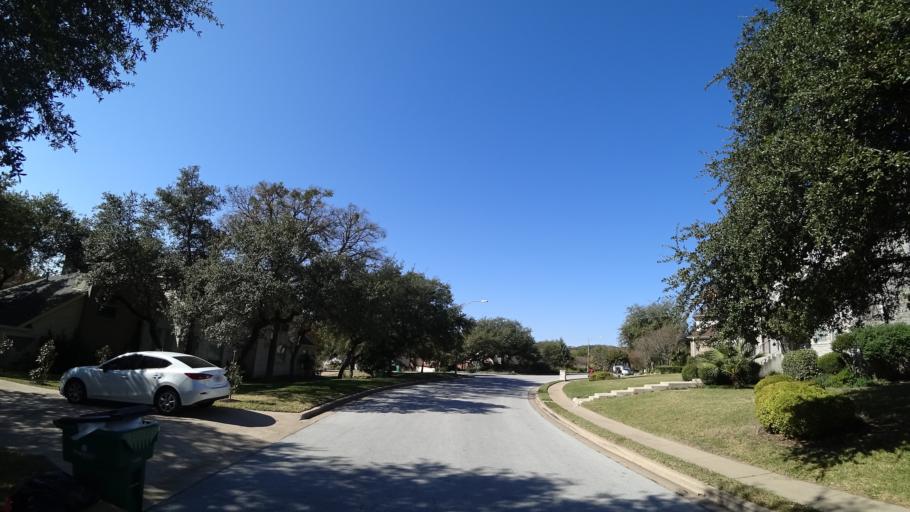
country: US
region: Texas
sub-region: Travis County
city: Lost Creek
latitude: 30.3669
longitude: -97.8625
